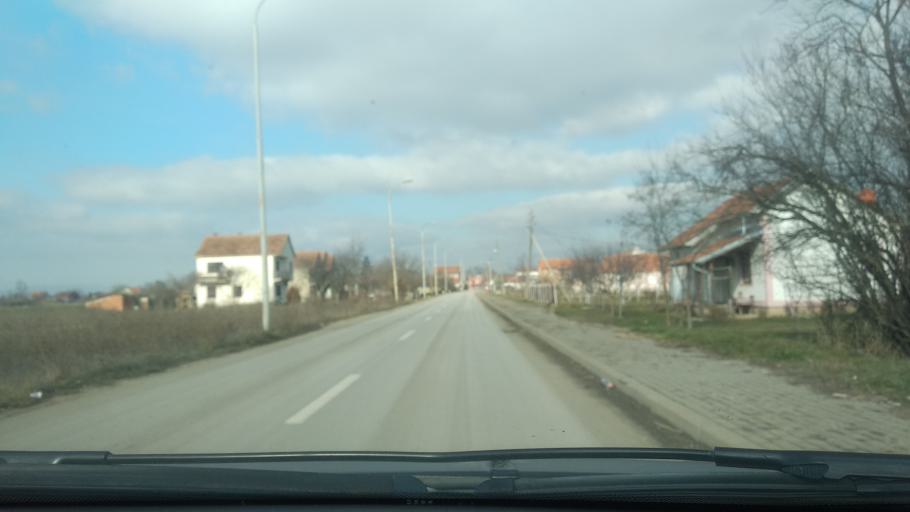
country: XK
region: Pristina
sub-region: Lipjan
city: Lipljan
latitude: 42.5906
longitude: 21.1498
